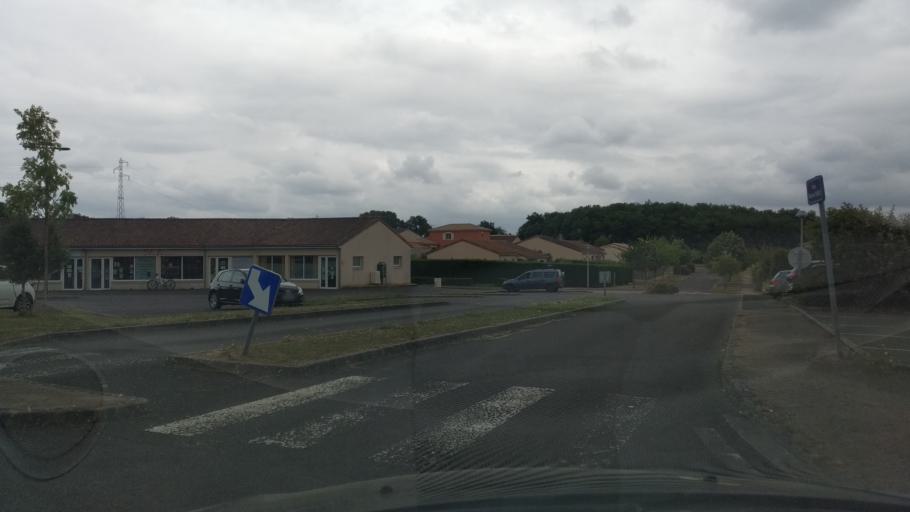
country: FR
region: Poitou-Charentes
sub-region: Departement de la Vienne
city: Smarves
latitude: 46.5103
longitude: 0.3538
